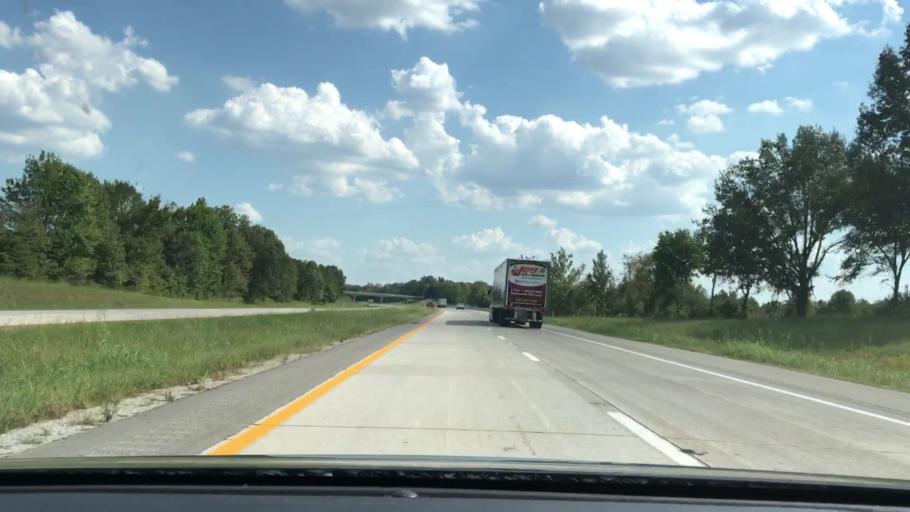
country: US
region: Kentucky
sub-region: Ohio County
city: Oak Grove
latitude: 37.3554
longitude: -86.7891
